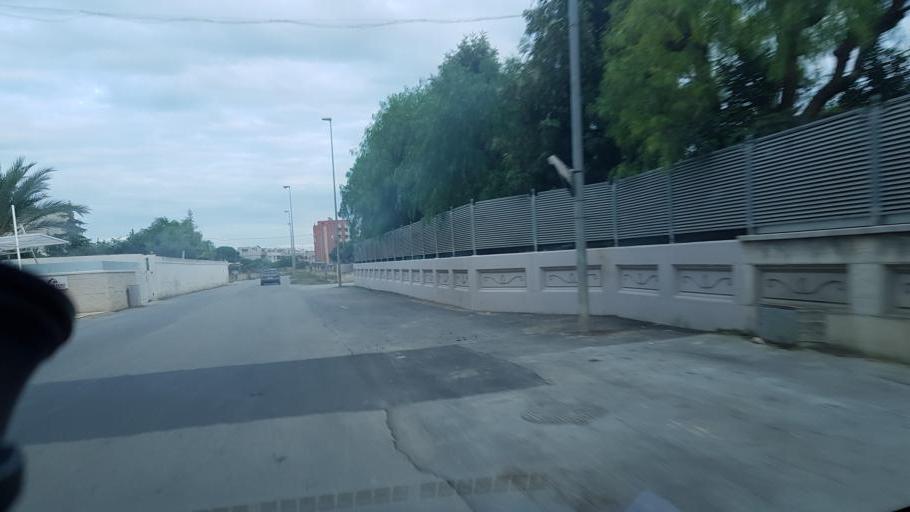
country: IT
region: Apulia
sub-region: Provincia di Brindisi
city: Latiano
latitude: 40.5483
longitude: 17.7239
